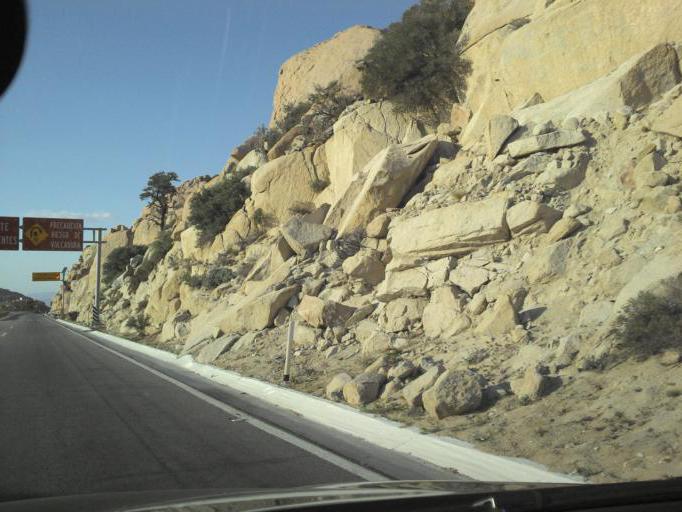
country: MX
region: Baja California
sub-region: Tecate
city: Cereso del Hongo
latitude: 32.5761
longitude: -116.0414
